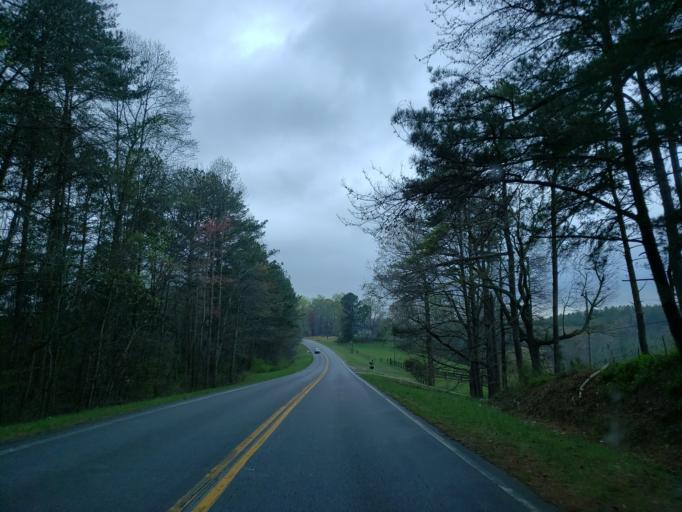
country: US
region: Georgia
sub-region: Polk County
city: Rockmart
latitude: 33.9221
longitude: -84.9786
